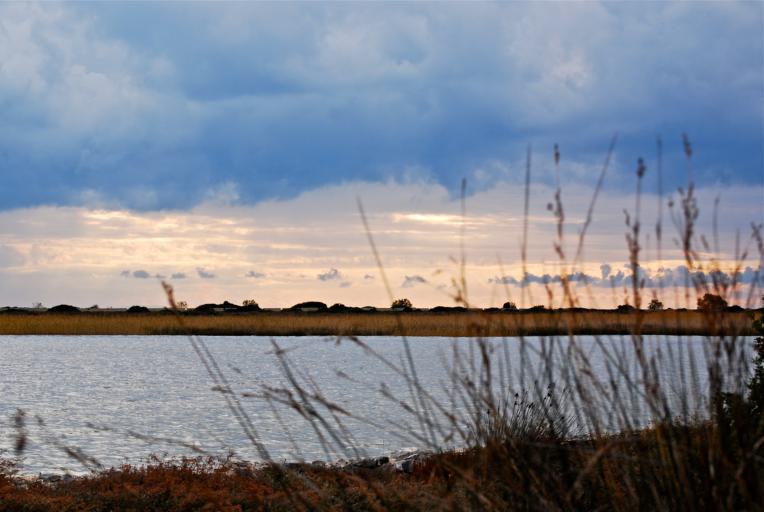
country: GR
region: North Aegean
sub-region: Nomos Samou
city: Vathy
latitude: 37.7080
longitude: 27.0108
